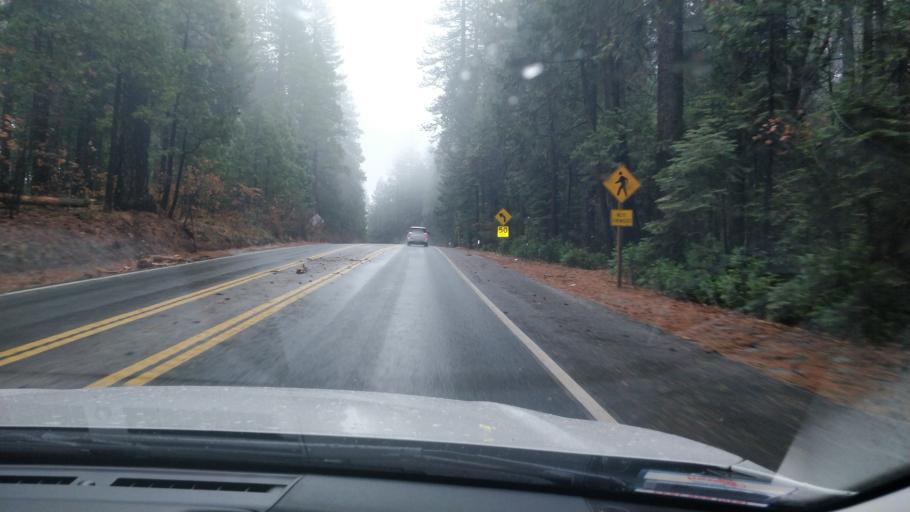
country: US
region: California
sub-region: Nevada County
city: Nevada City
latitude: 39.3210
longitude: -120.8480
